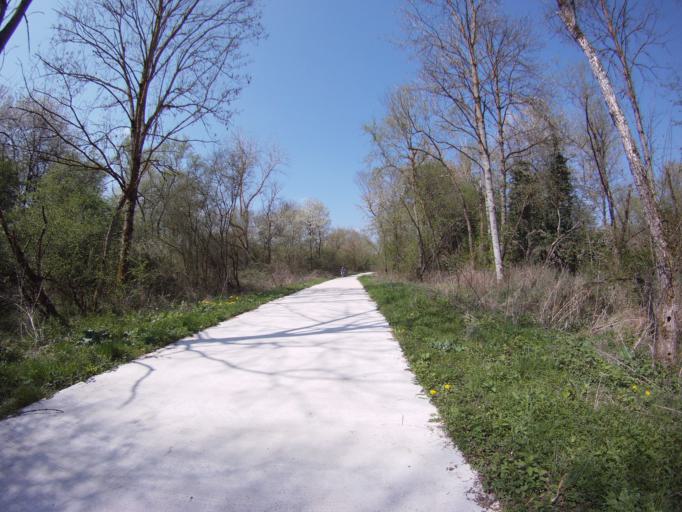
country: FR
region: Lorraine
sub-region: Departement de Meurthe-et-Moselle
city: Dieulouard
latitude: 48.8411
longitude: 6.0888
